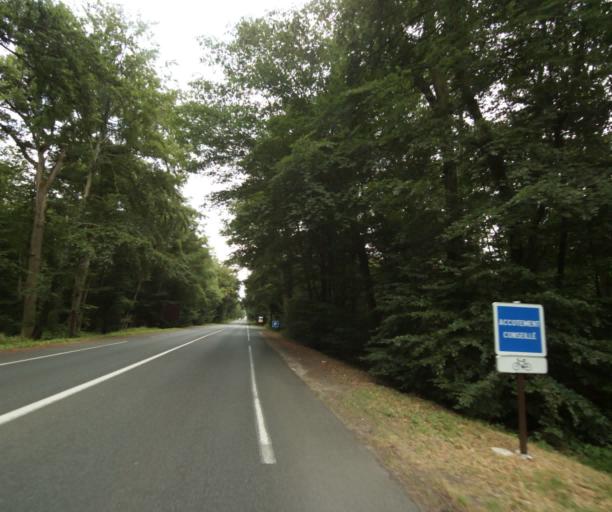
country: FR
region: Ile-de-France
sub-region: Departement de Seine-et-Marne
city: Bois-le-Roi
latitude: 48.4737
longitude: 2.6789
